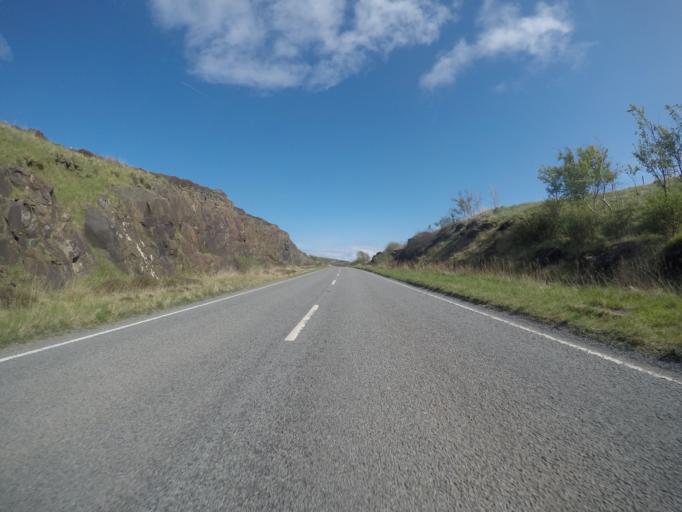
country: GB
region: Scotland
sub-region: Highland
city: Portree
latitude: 57.6153
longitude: -6.1862
